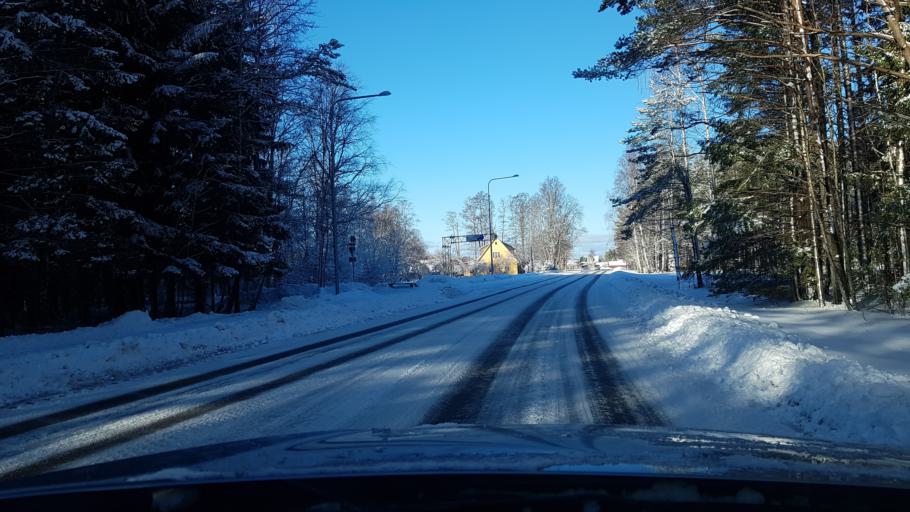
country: EE
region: Hiiumaa
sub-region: Kaerdla linn
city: Kardla
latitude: 58.9824
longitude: 22.7580
